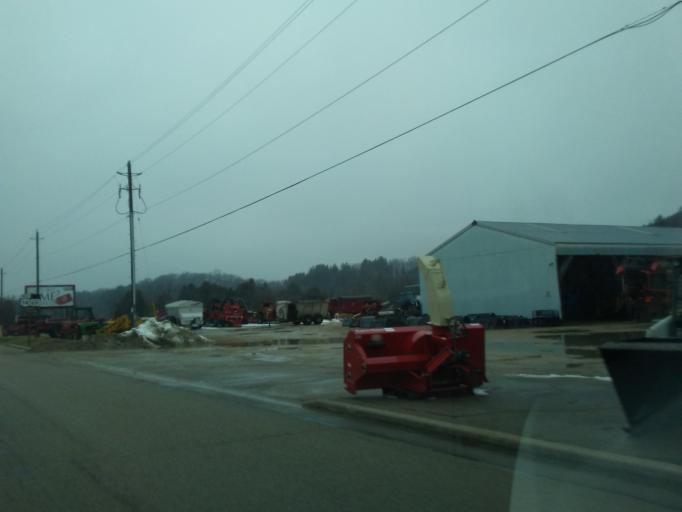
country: US
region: Wisconsin
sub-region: Dane County
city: Cross Plains
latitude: 43.1148
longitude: -89.6612
